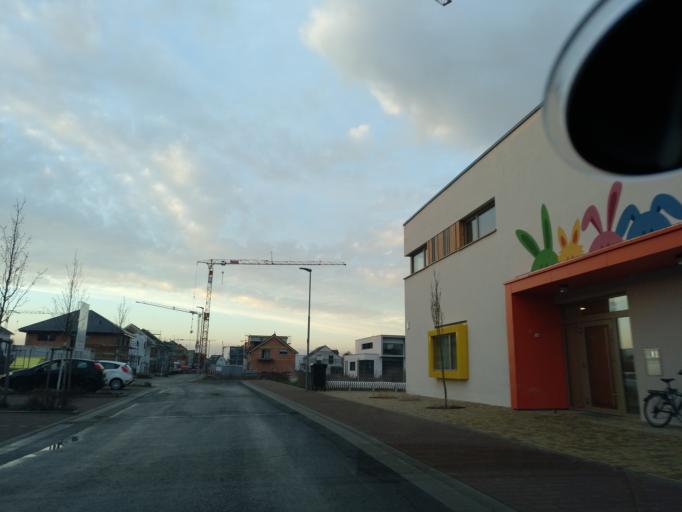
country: DE
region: Baden-Wuerttemberg
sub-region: Karlsruhe Region
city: Reilingen
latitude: 49.2958
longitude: 8.5749
